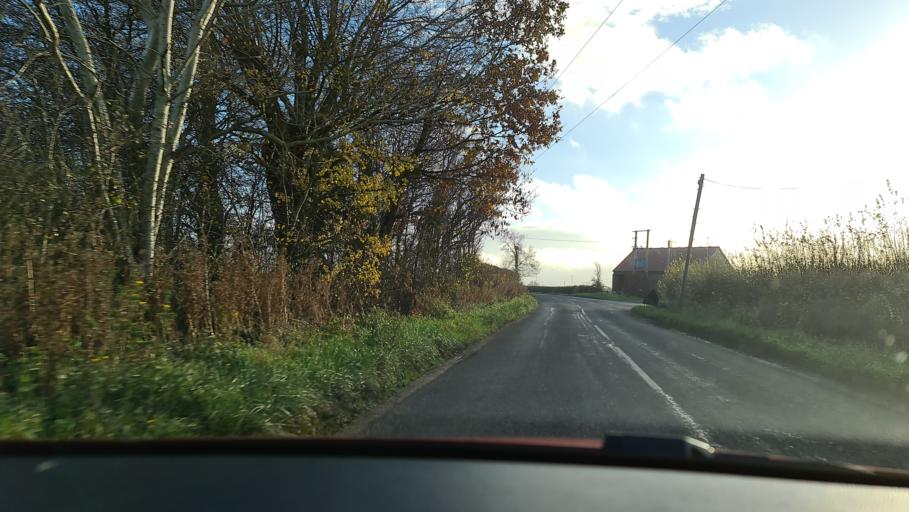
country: GB
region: England
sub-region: Buckinghamshire
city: Aylesbury
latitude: 51.7815
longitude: -0.8208
